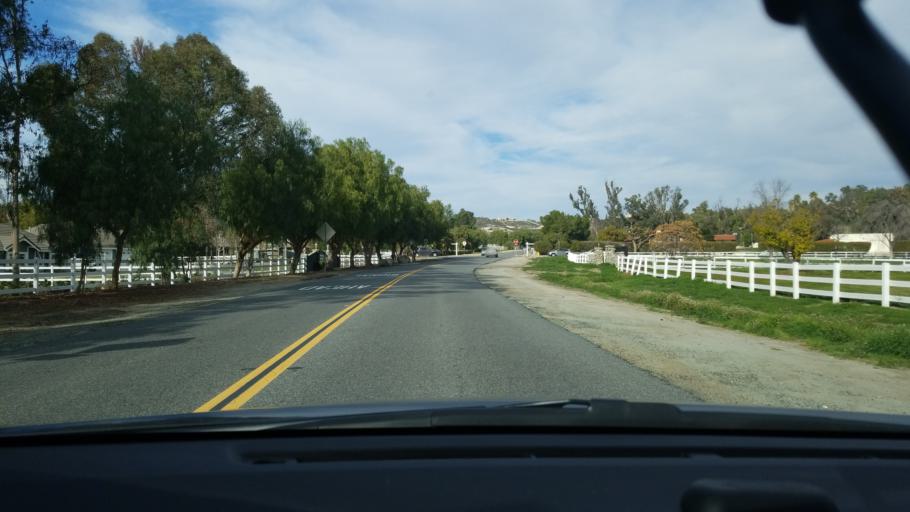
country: US
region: California
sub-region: Riverside County
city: Temecula
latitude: 33.4773
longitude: -117.1228
